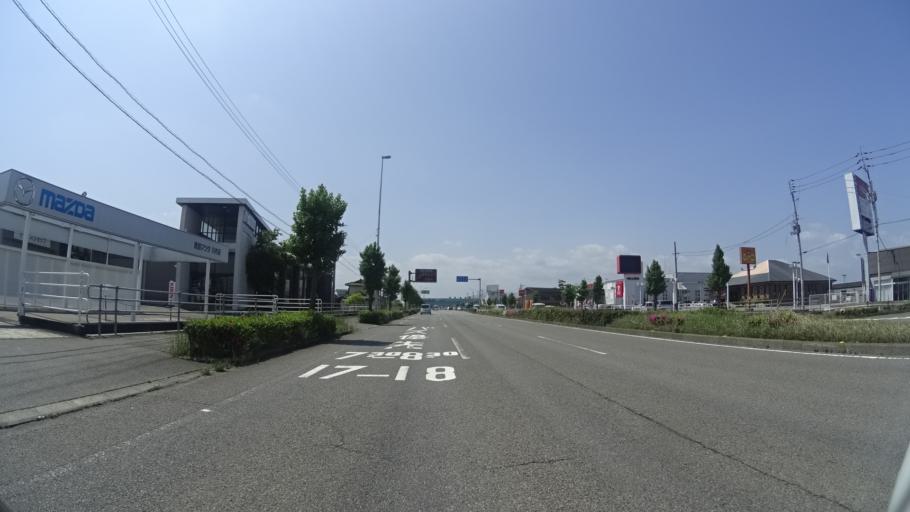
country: JP
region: Tokushima
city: Tokushima-shi
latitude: 34.1077
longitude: 134.5766
